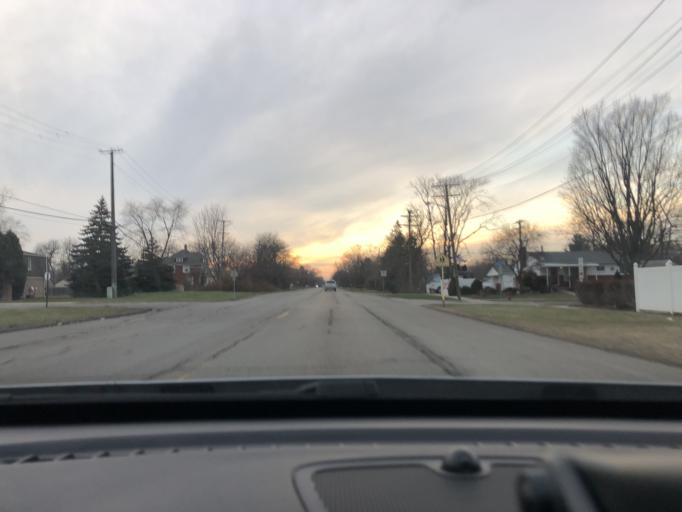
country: US
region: Michigan
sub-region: Wayne County
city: Allen Park
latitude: 42.2421
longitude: -83.2335
